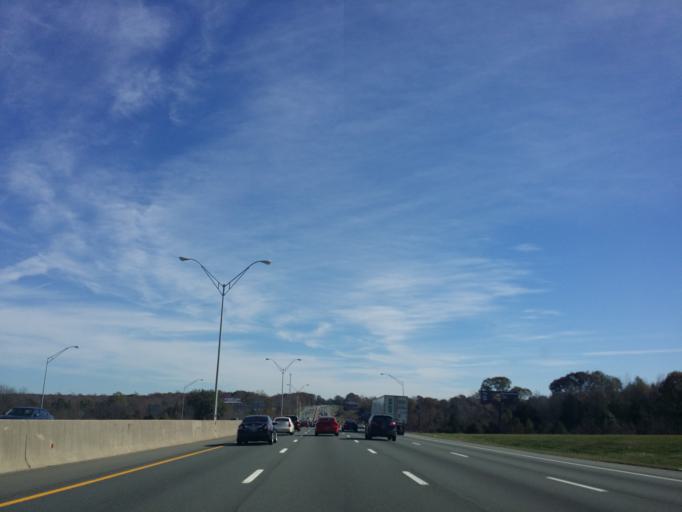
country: US
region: North Carolina
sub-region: Alamance County
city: Haw River
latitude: 36.0687
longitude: -79.3512
